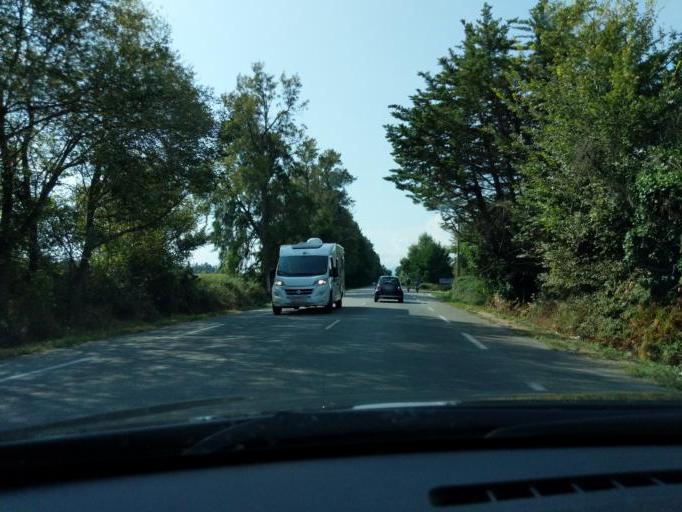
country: FR
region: Corsica
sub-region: Departement de la Haute-Corse
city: Ghisonaccia
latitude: 41.9731
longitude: 9.3989
